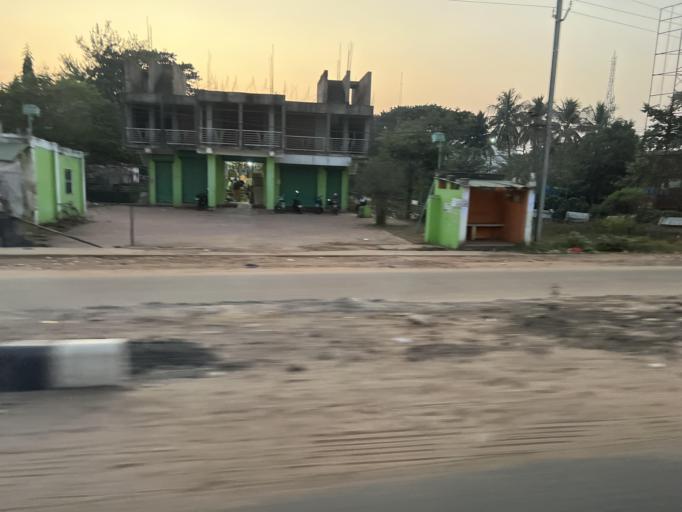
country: IN
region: Odisha
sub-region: Cuttack
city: Cuttack
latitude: 20.3962
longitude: 85.8820
